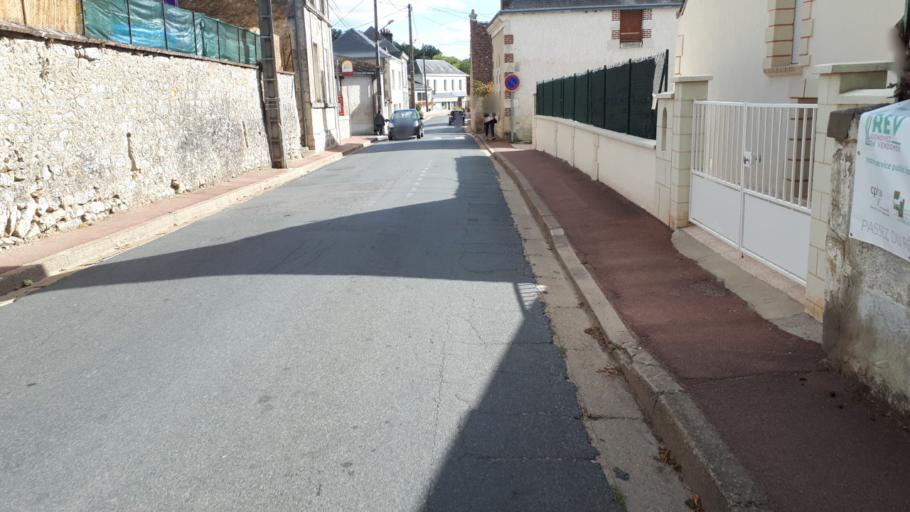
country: FR
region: Centre
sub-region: Departement du Loir-et-Cher
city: Villiers-sur-Loir
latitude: 47.7883
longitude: 0.9631
